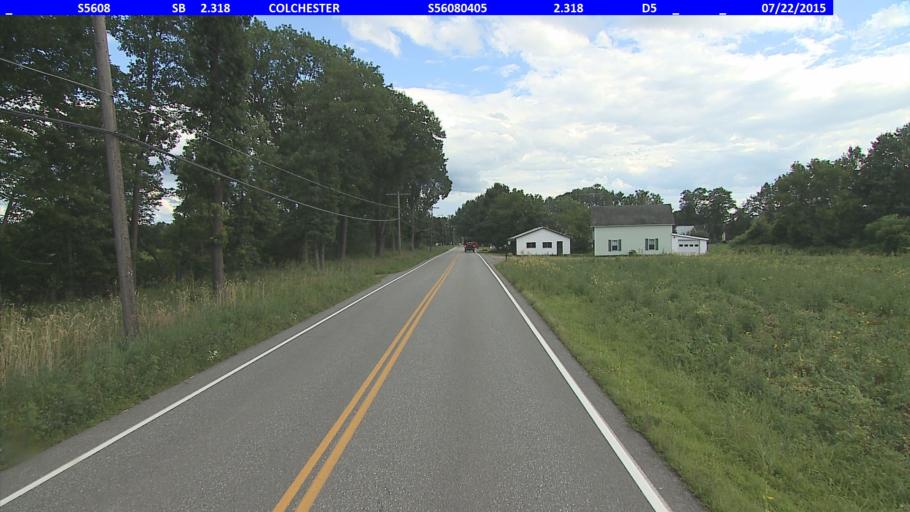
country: US
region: Vermont
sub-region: Chittenden County
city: Winooski
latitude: 44.5302
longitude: -73.2076
